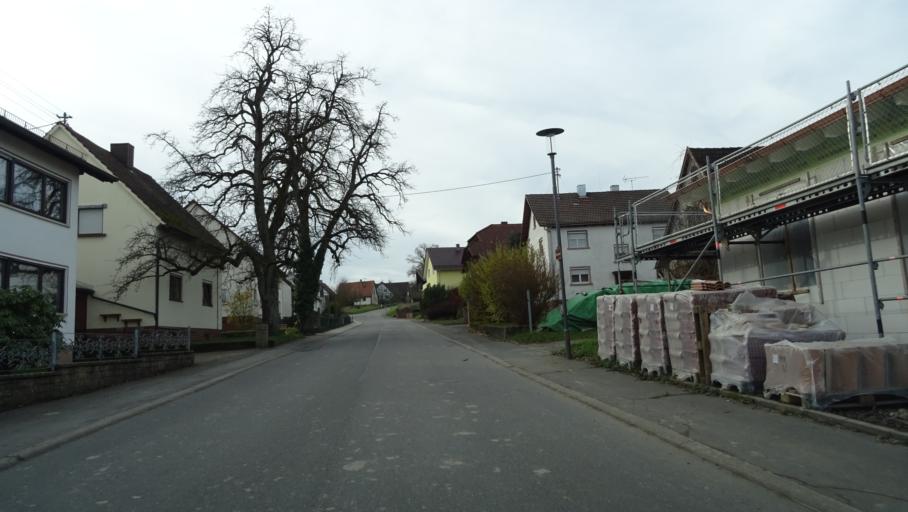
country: DE
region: Baden-Wuerttemberg
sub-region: Karlsruhe Region
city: Fahrenbach
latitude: 49.4082
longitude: 9.1665
